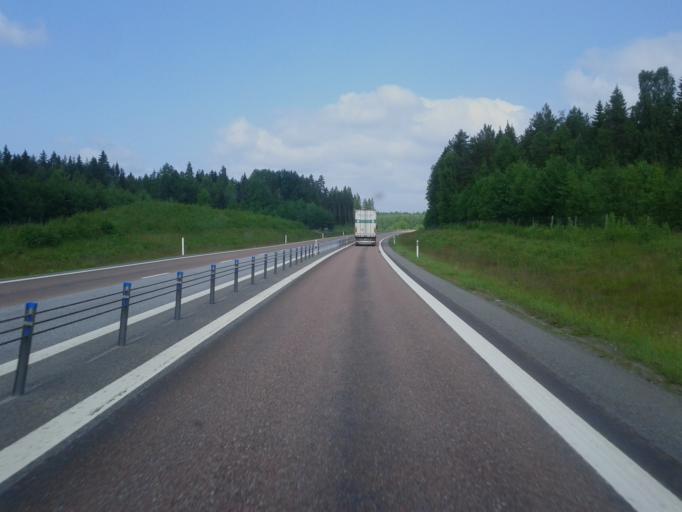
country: SE
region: Vaesterbotten
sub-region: Skelleftea Kommun
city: Skelleftea
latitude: 64.7183
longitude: 20.9884
